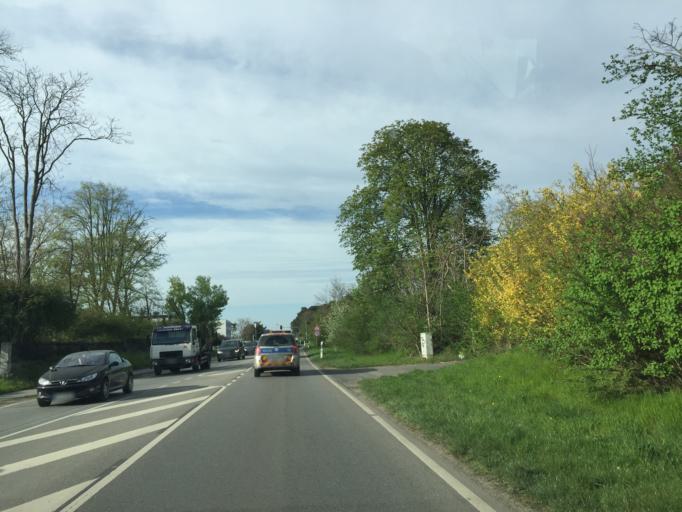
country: DE
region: Hesse
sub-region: Regierungsbezirk Darmstadt
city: Alsbach-Hahnlein
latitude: 49.7437
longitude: 8.6095
